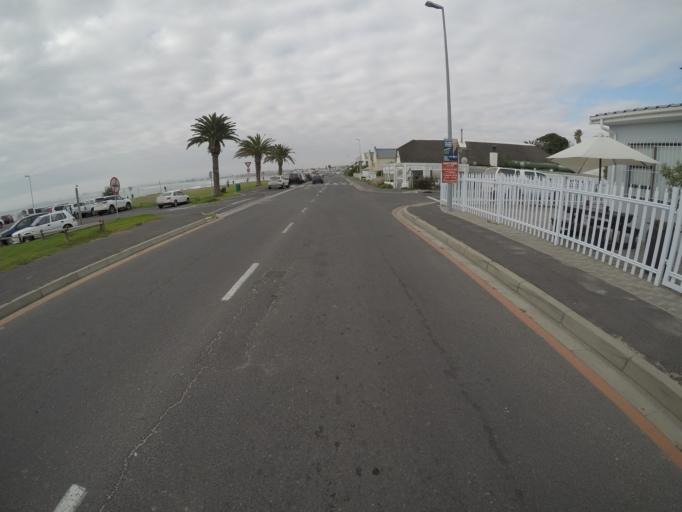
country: ZA
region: Western Cape
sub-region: City of Cape Town
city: Sunset Beach
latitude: -33.7288
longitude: 18.4396
